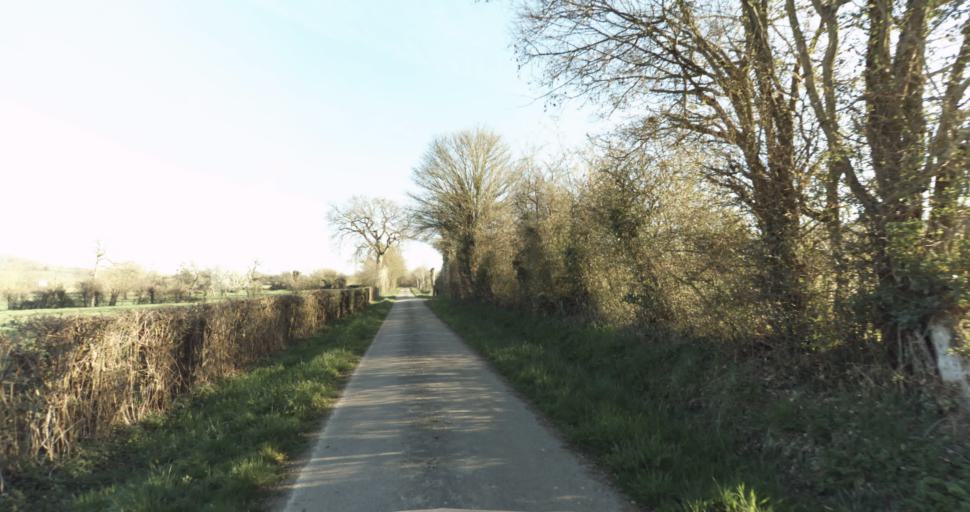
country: FR
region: Lower Normandy
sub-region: Departement de l'Orne
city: Trun
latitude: 48.9061
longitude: 0.0177
